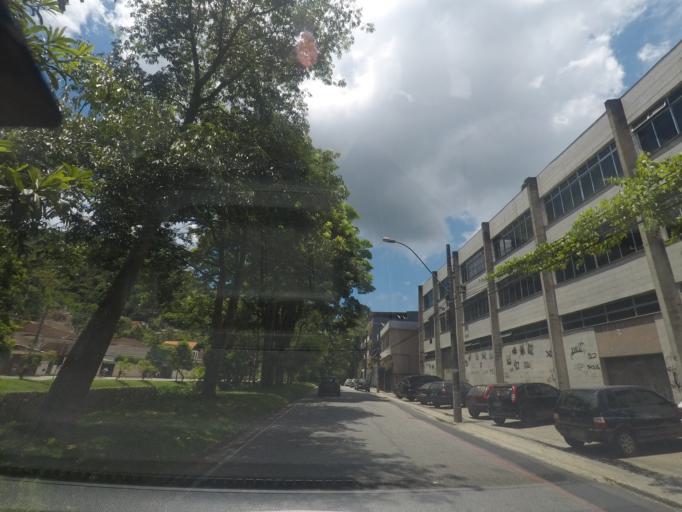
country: BR
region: Rio de Janeiro
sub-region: Petropolis
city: Petropolis
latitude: -22.4937
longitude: -43.1798
